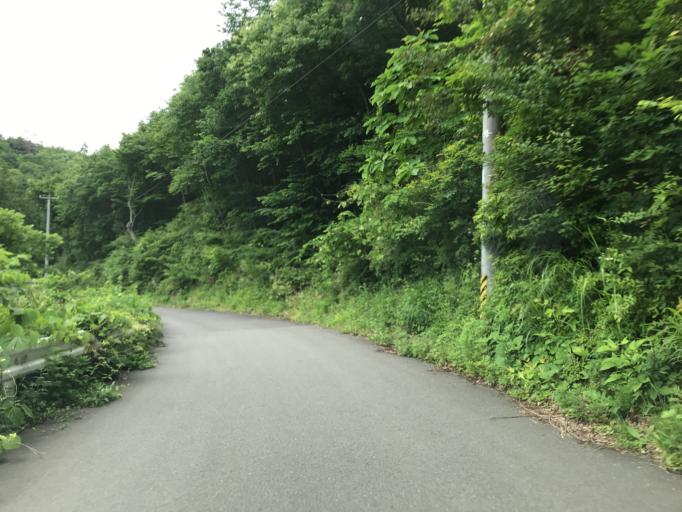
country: JP
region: Fukushima
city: Funehikimachi-funehiki
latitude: 37.4413
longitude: 140.7783
